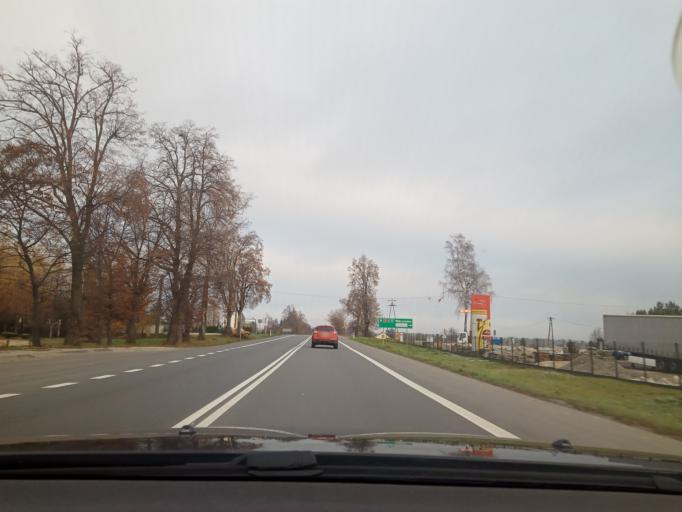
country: PL
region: Lesser Poland Voivodeship
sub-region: Powiat miechowski
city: Miechow
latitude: 50.3339
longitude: 20.0341
